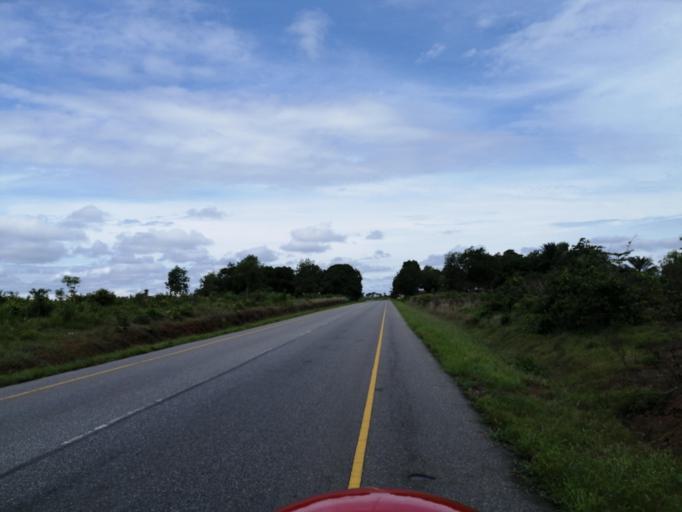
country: SL
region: Northern Province
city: Port Loko
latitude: 8.7374
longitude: -12.9456
